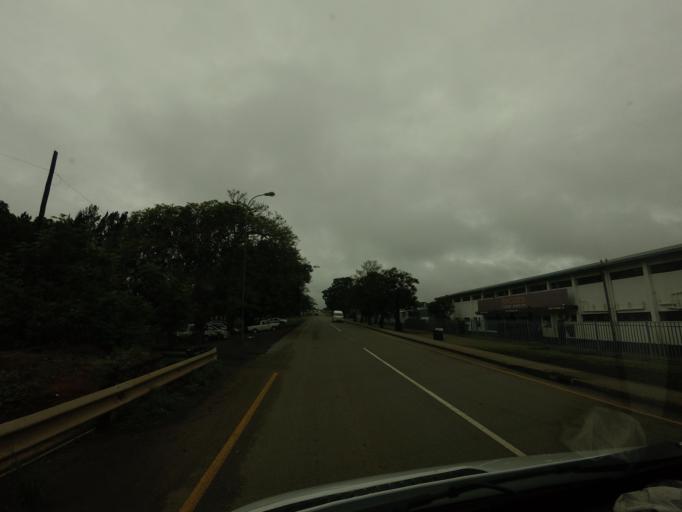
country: SZ
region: Manzini
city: Malkerns
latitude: -26.5197
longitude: 31.1960
